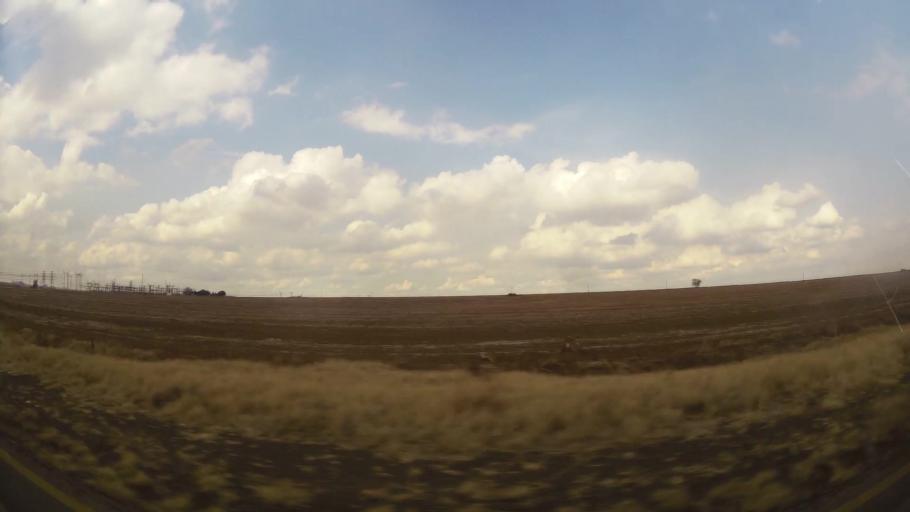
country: ZA
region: Orange Free State
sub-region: Fezile Dabi District Municipality
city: Sasolburg
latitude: -26.8254
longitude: 27.9019
